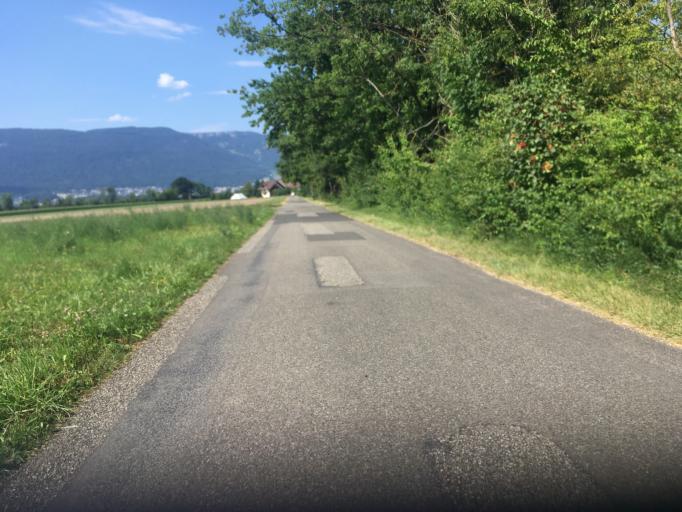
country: CH
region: Bern
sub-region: Biel/Bienne District
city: Lengnau
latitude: 47.1542
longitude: 7.3868
